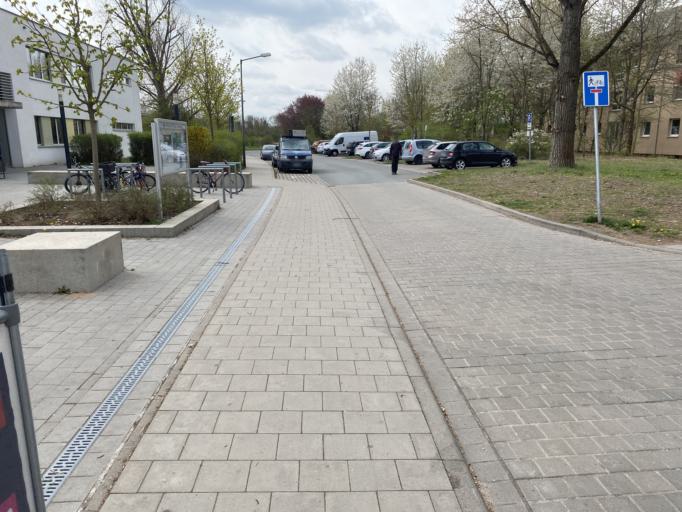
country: DE
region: Bavaria
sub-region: Regierungsbezirk Mittelfranken
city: Erlangen
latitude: 49.5865
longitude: 11.0241
